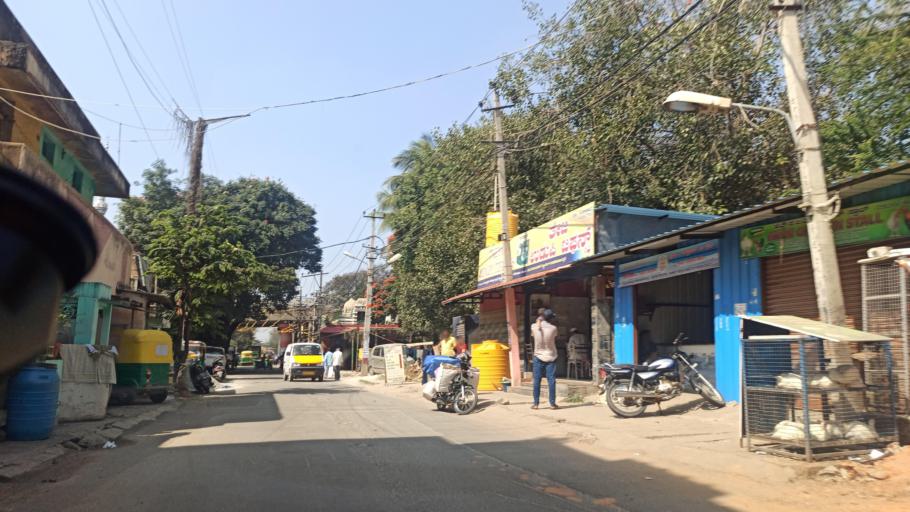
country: IN
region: Karnataka
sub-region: Bangalore Urban
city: Yelahanka
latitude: 13.0409
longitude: 77.5910
